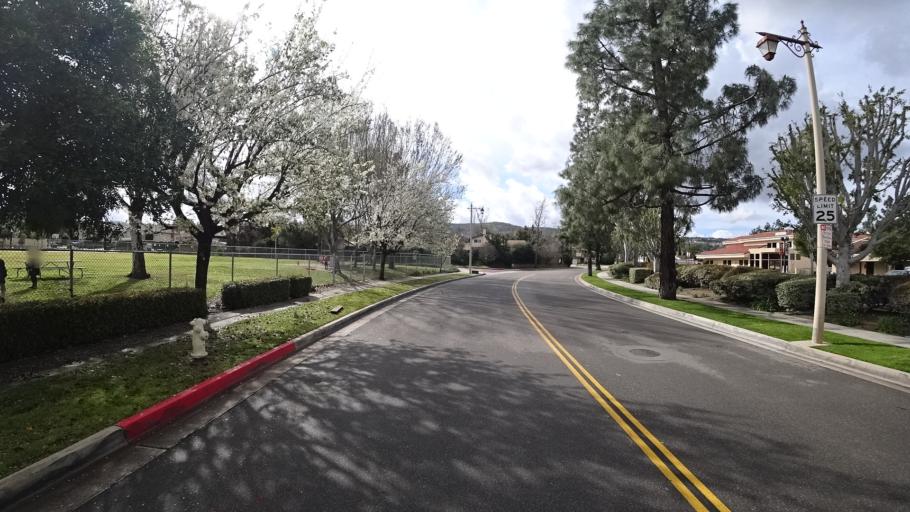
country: US
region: California
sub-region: Orange County
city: Villa Park
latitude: 33.8512
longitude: -117.7836
